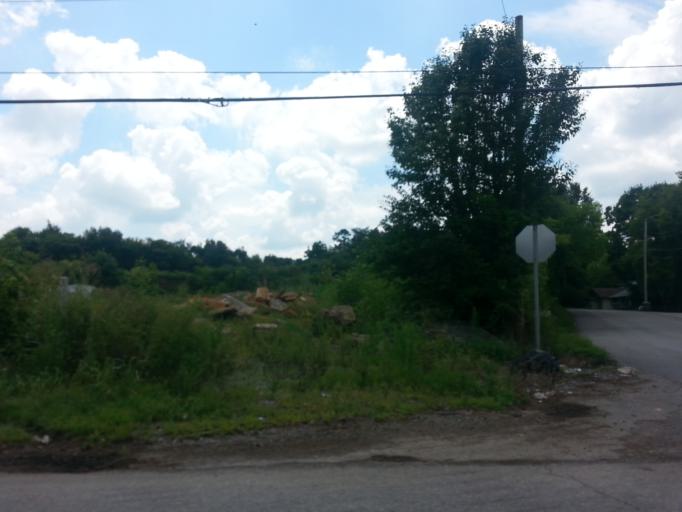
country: US
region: Tennessee
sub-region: Blount County
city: Alcoa
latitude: 35.7802
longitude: -83.9538
